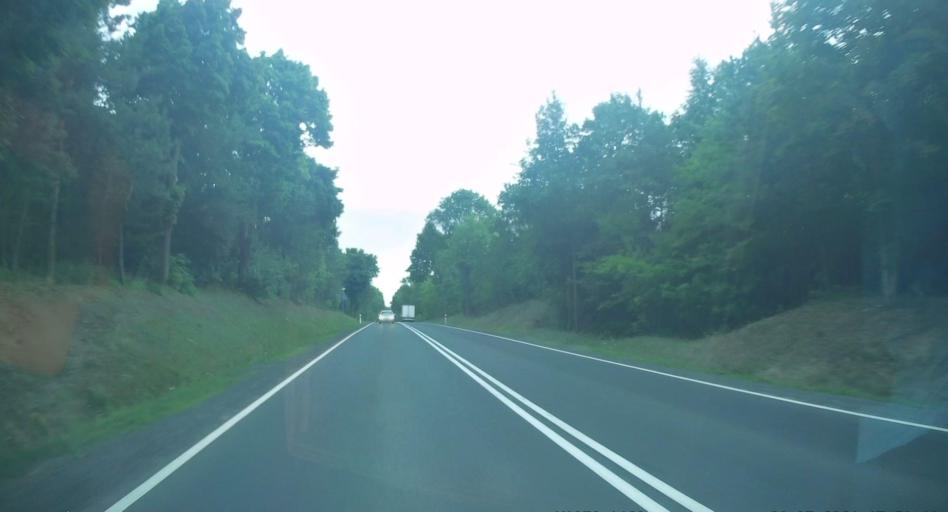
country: PL
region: Lodz Voivodeship
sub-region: Powiat radomszczanski
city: Gomunice
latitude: 51.1800
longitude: 19.4956
